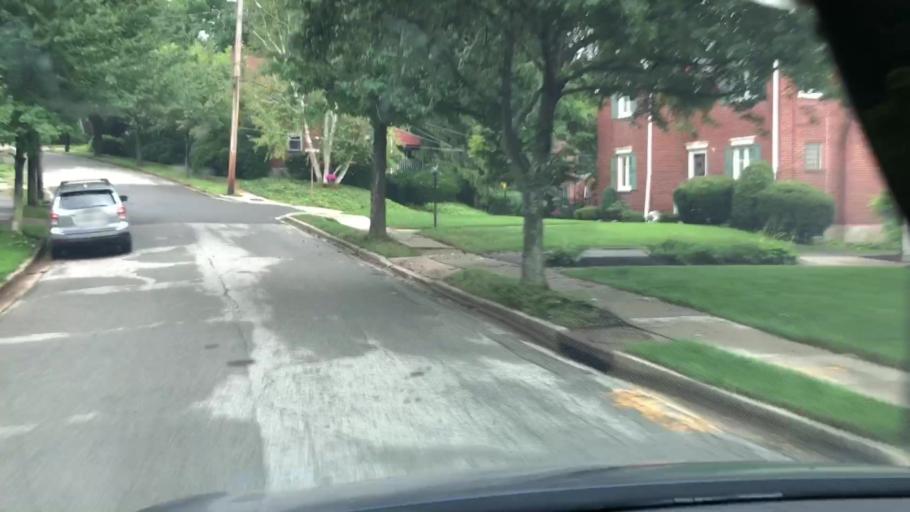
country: US
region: Pennsylvania
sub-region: Allegheny County
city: Dormont
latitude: 40.3812
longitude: -80.0342
